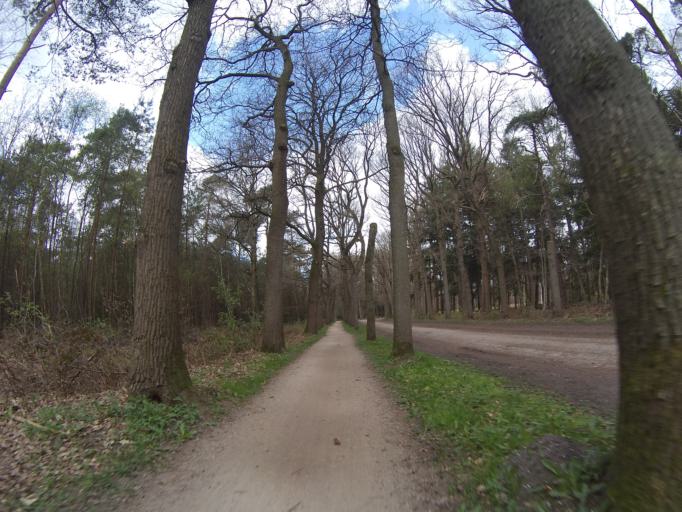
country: NL
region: Utrecht
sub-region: Gemeente Soest
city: Soest
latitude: 52.1785
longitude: 5.2378
